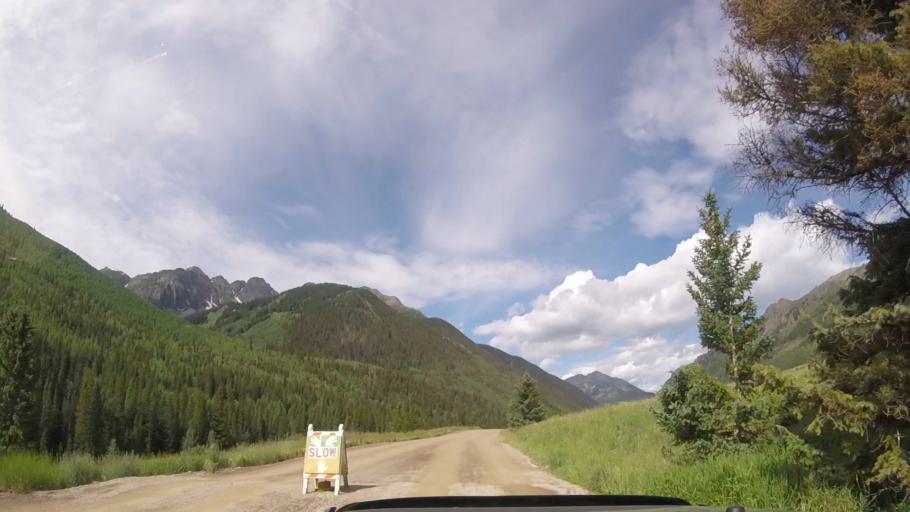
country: US
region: Colorado
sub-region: San Miguel County
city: Mountain Village
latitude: 37.8558
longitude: -107.8261
